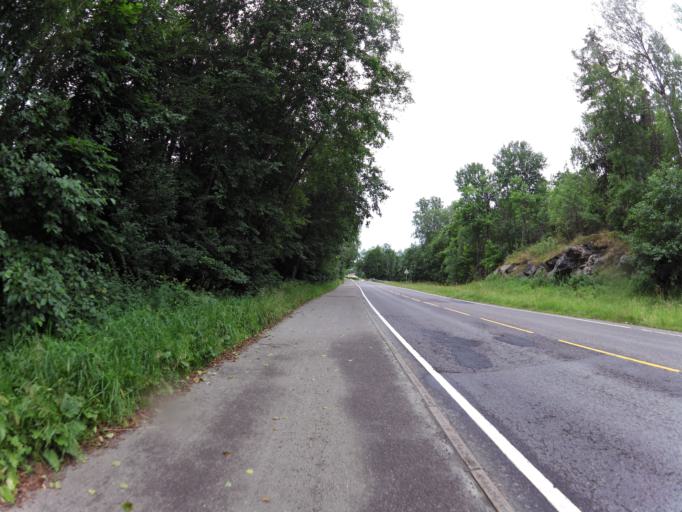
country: NO
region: Ostfold
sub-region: Moss
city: Moss
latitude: 59.4761
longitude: 10.6945
